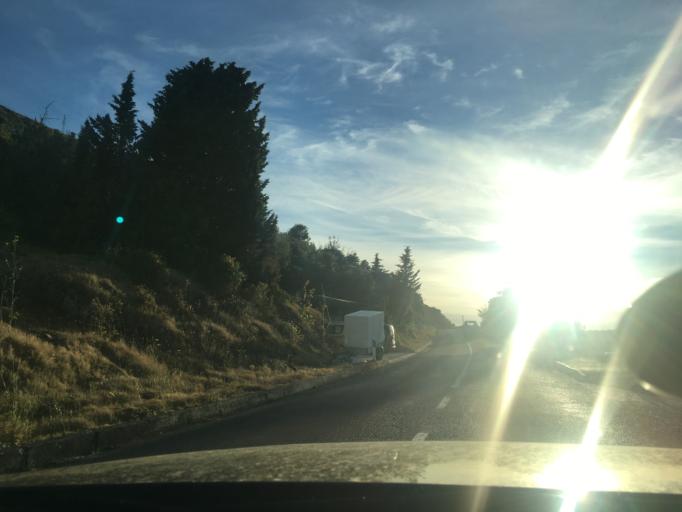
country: HR
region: Splitsko-Dalmatinska
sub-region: Grad Vis
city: Vis
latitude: 43.0576
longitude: 16.1890
